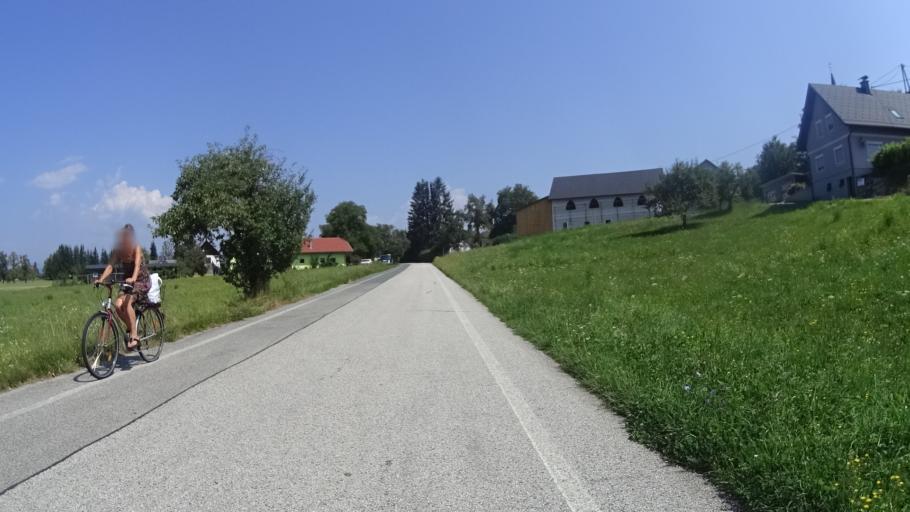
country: AT
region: Carinthia
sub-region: Politischer Bezirk Volkermarkt
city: Eberndorf
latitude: 46.5722
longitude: 14.6323
